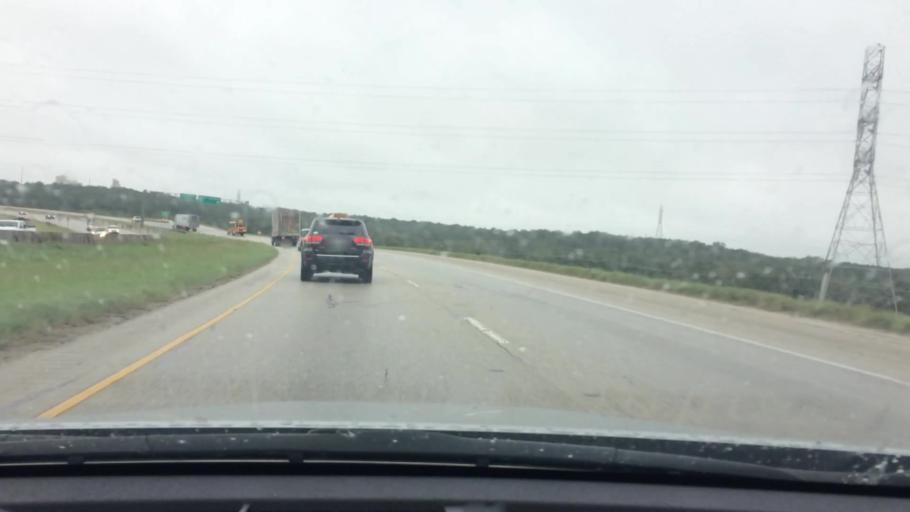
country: US
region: Texas
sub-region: Bexar County
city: Live Oak
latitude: 29.6016
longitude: -98.3598
